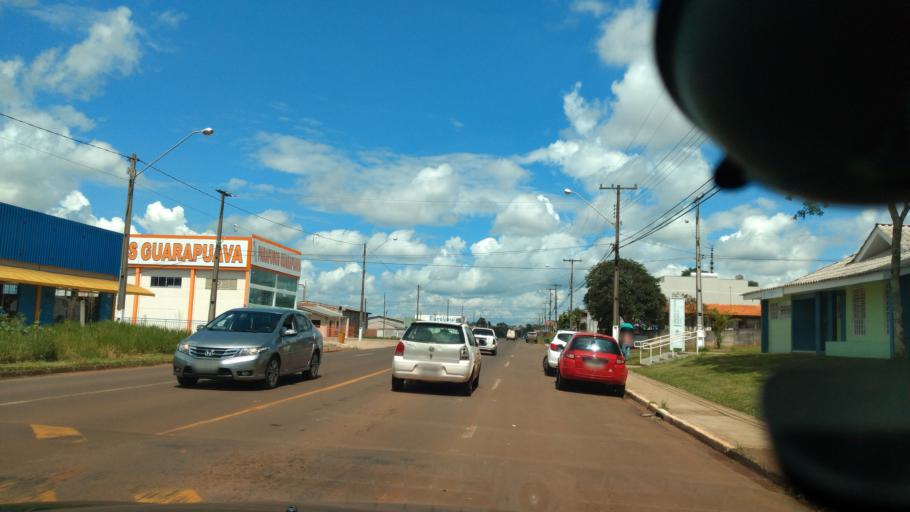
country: BR
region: Parana
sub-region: Guarapuava
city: Guarapuava
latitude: -25.3931
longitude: -51.4946
